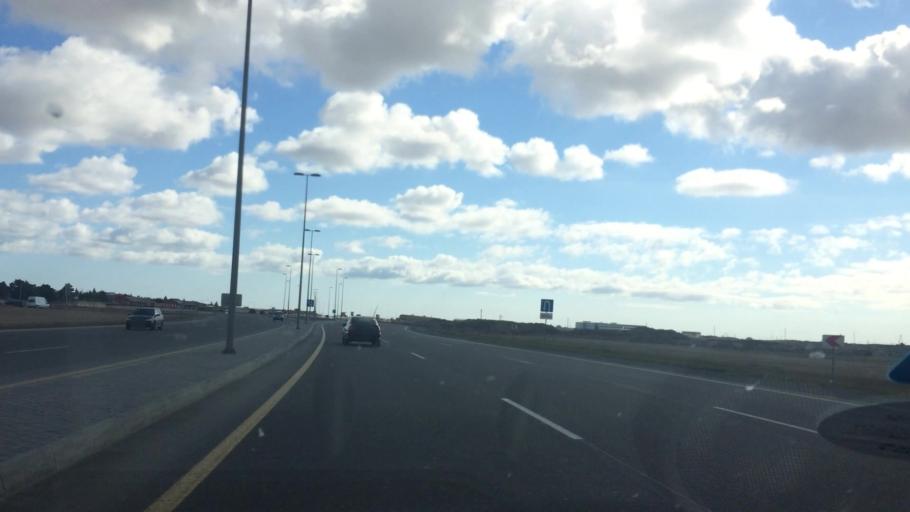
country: AZ
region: Baki
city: Mardakyany
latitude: 40.4586
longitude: 50.1300
